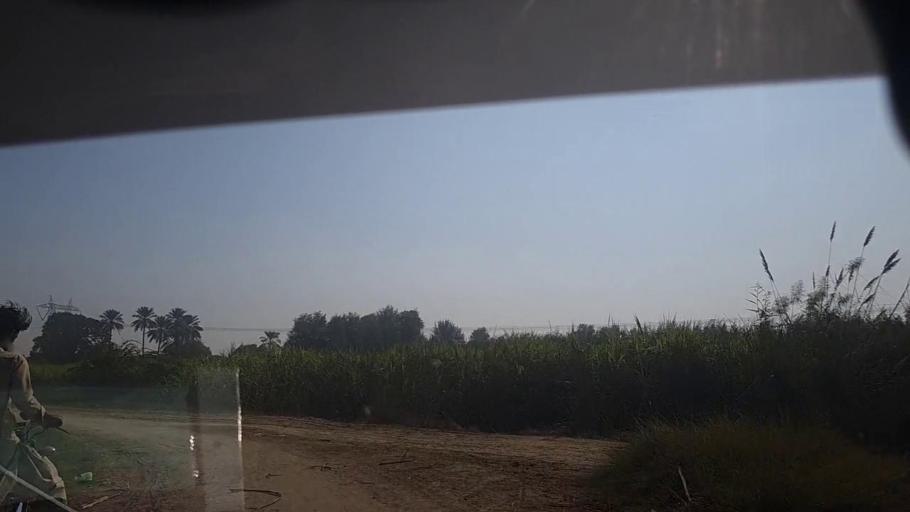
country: PK
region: Sindh
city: Khairpur
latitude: 27.4580
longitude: 68.7415
